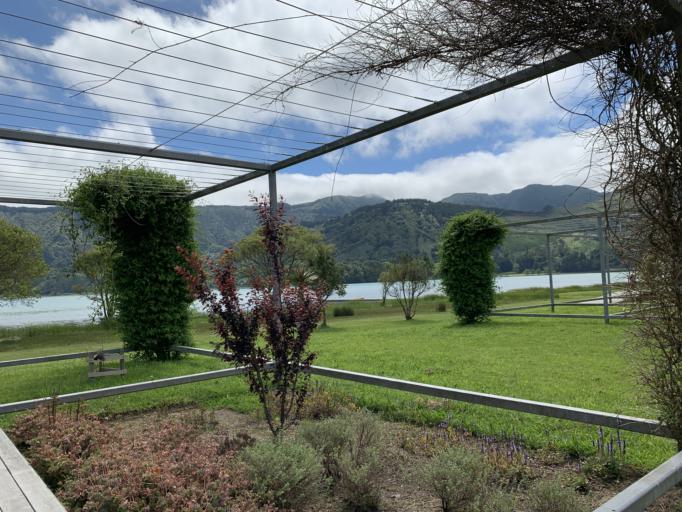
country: PT
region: Azores
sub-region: Ponta Delgada
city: Arrifes
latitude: 37.8629
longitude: -25.7924
